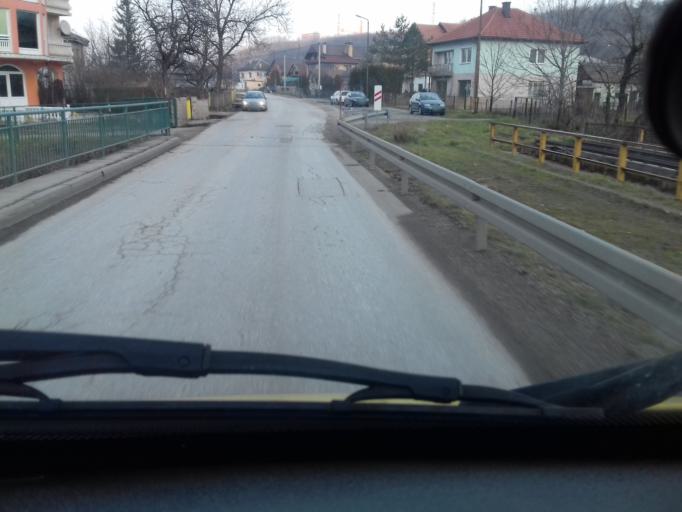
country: BA
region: Federation of Bosnia and Herzegovina
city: Kakanj
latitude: 44.0986
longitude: 18.1087
